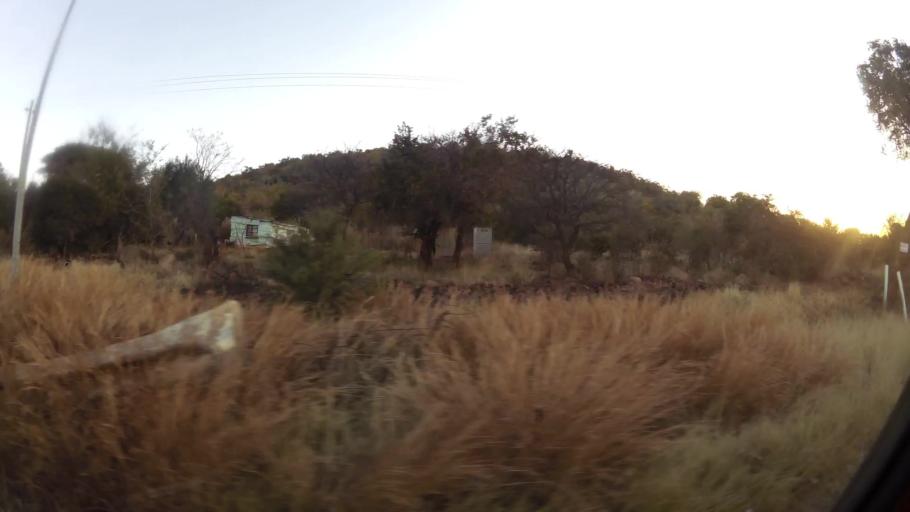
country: ZA
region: North-West
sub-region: Bojanala Platinum District Municipality
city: Rustenburg
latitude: -25.6214
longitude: 27.1957
